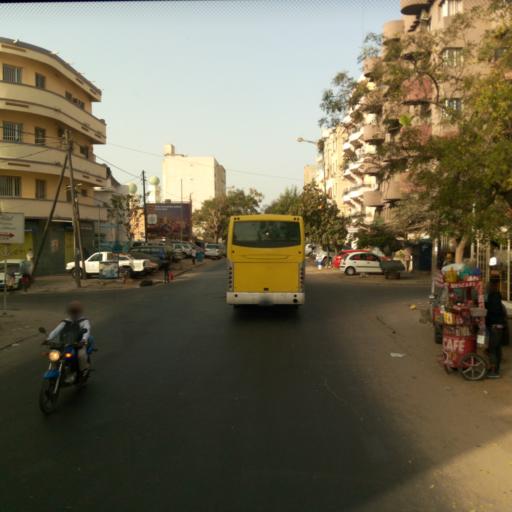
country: SN
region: Dakar
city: Dakar
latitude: 14.6760
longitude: -17.4470
